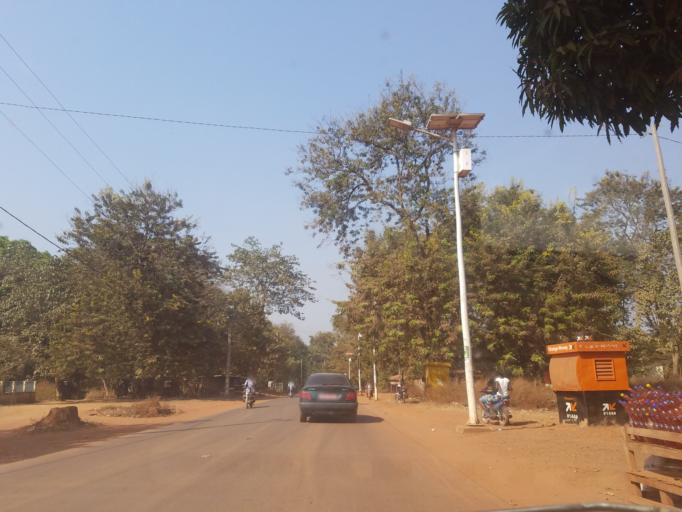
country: GN
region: Boke
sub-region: Boke Prefecture
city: Boke
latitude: 10.9228
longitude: -14.2955
